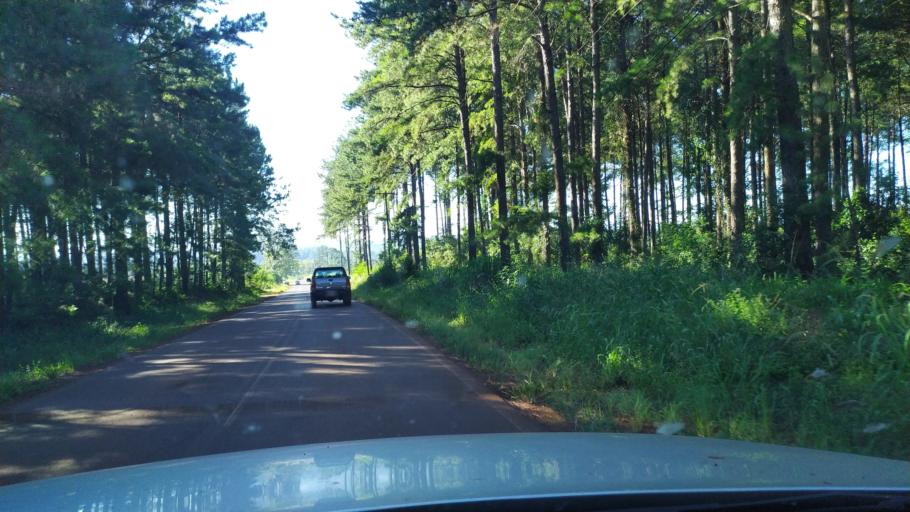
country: AR
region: Misiones
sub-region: Departamento de Montecarlo
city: Montecarlo
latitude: -26.5865
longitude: -54.7234
